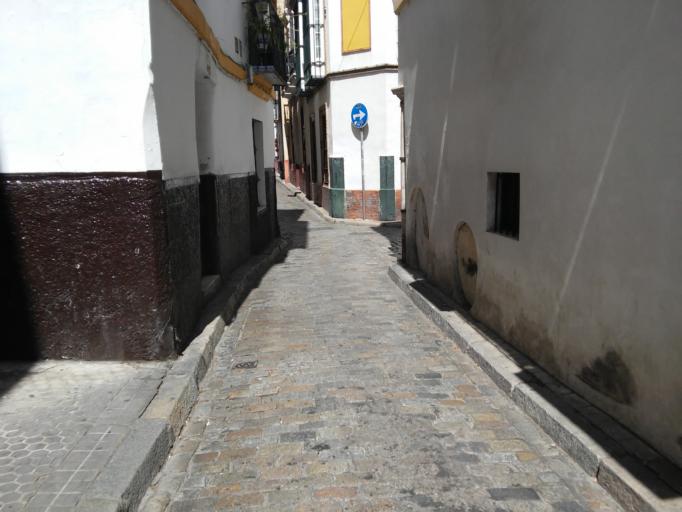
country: ES
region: Andalusia
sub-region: Provincia de Sevilla
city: Sevilla
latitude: 37.3882
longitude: -5.9913
